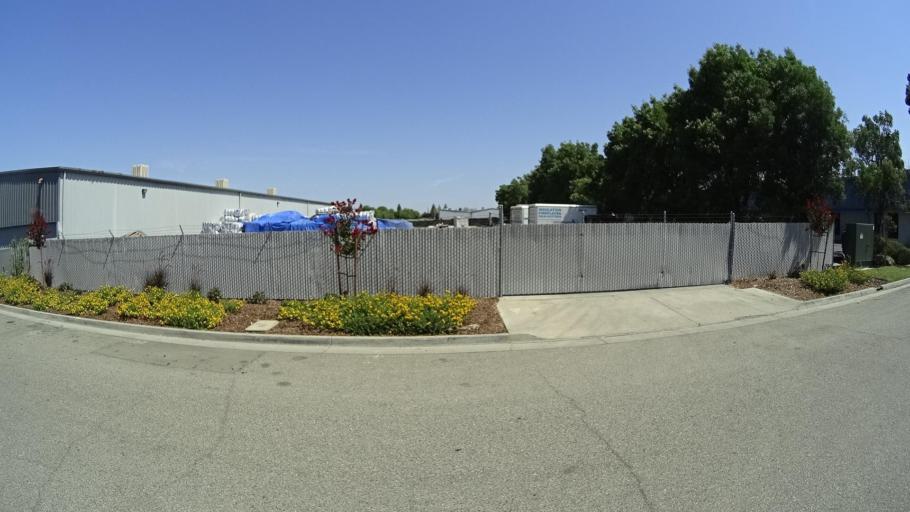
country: US
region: California
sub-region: Fresno County
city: Tarpey Village
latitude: 36.7749
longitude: -119.6886
